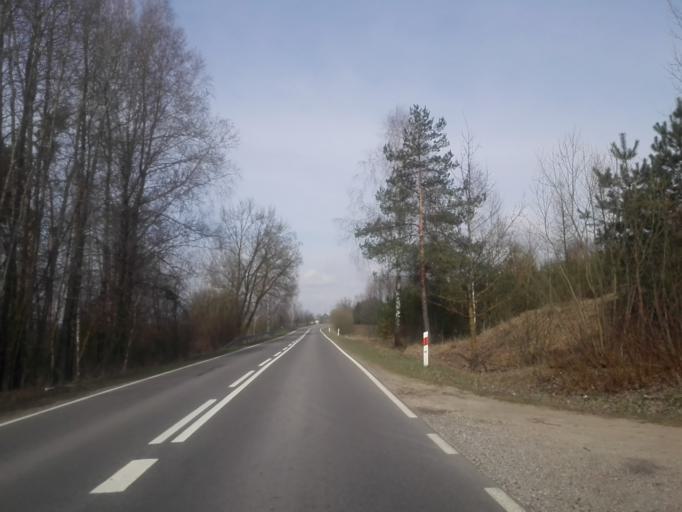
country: PL
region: Podlasie
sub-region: Powiat sejnenski
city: Sejny
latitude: 54.0713
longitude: 23.3528
